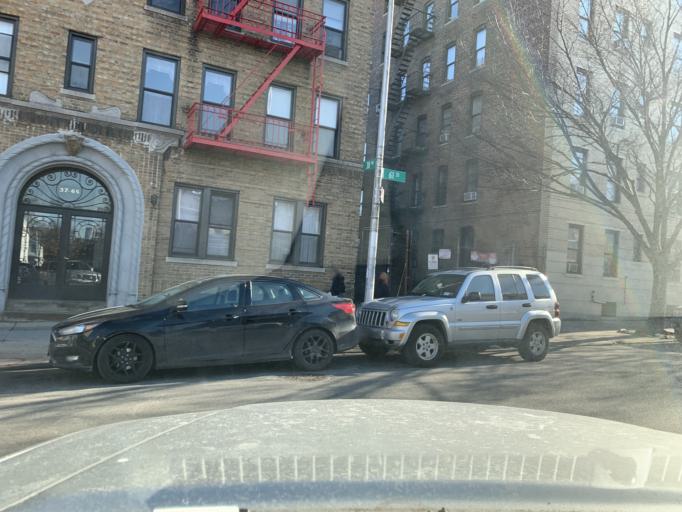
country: US
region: New York
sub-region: Queens County
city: Long Island City
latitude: 40.7477
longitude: -73.9025
